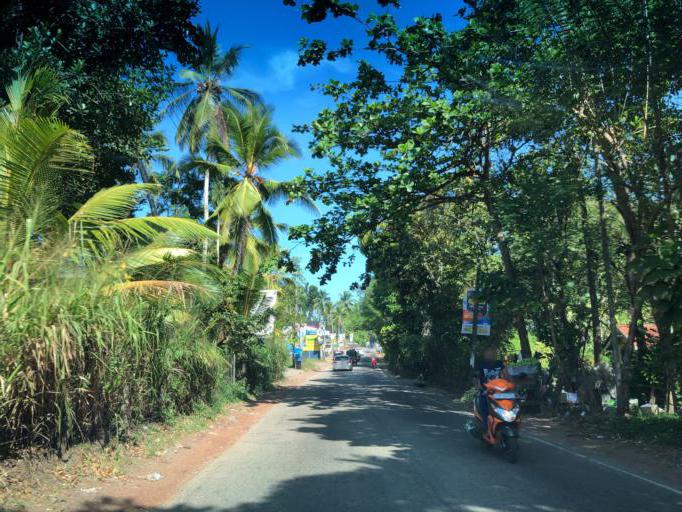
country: LK
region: Western
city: Homagama
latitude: 6.8292
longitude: 79.9655
